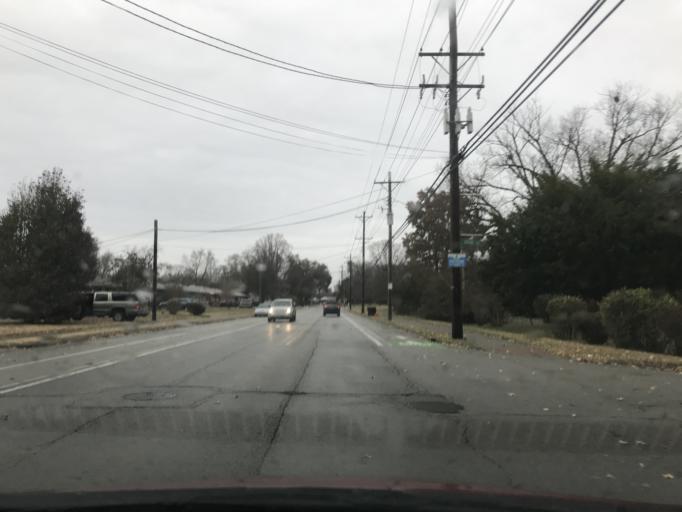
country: US
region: Kentucky
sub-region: Jefferson County
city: West Buechel
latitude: 38.2110
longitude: -85.6642
